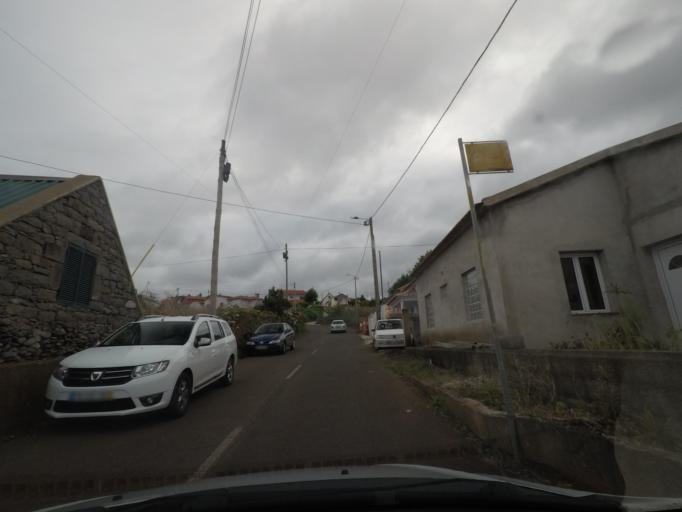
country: PT
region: Madeira
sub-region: Santana
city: Santana
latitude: 32.7922
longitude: -16.8729
